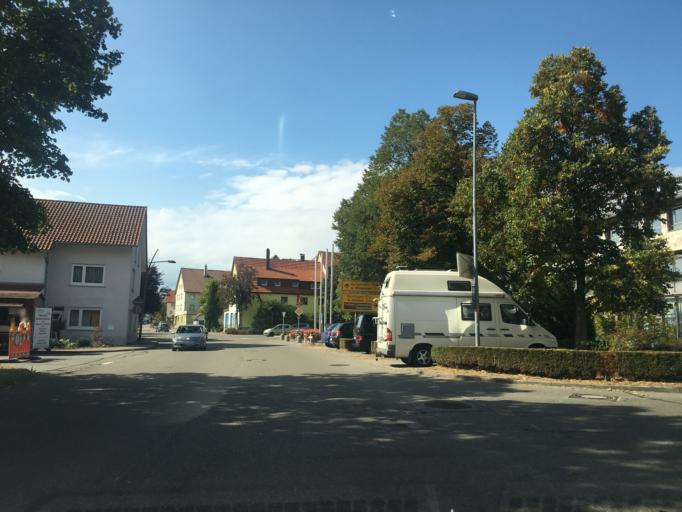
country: DE
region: Baden-Wuerttemberg
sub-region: Tuebingen Region
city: Pfullingen
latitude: 48.3894
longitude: 9.1804
